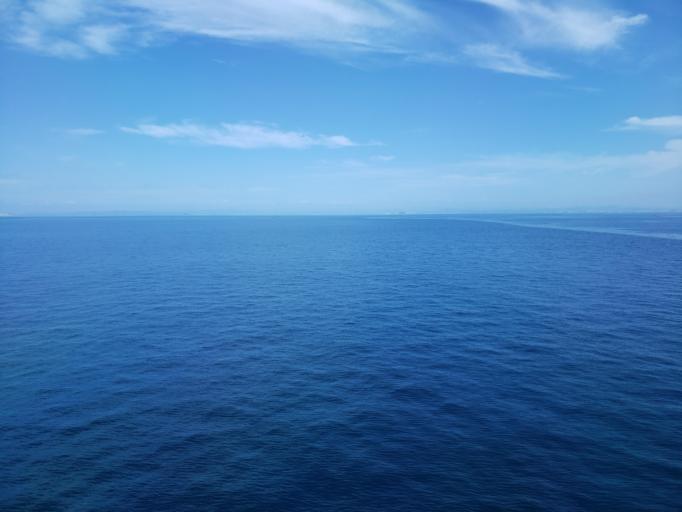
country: JP
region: Hyogo
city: Kakogawacho-honmachi
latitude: 34.5545
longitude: 134.7492
